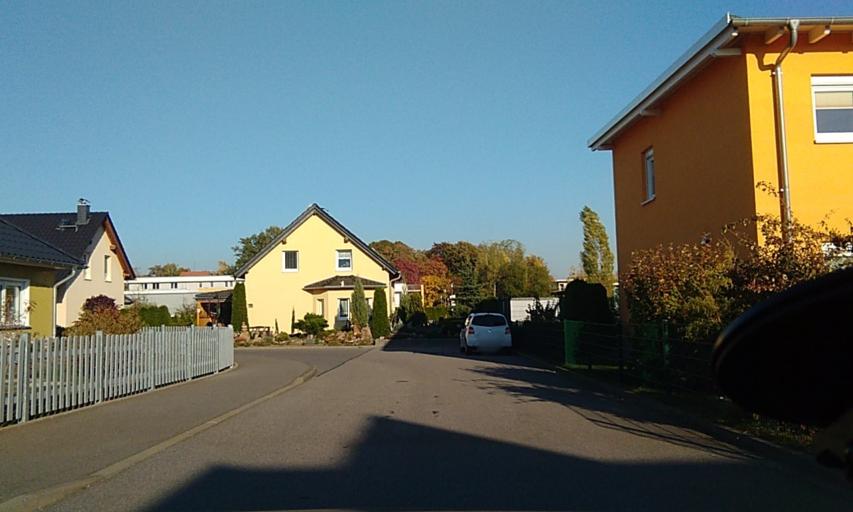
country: DE
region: Saxony
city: Wittgensdorf
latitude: 50.8443
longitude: 12.8708
